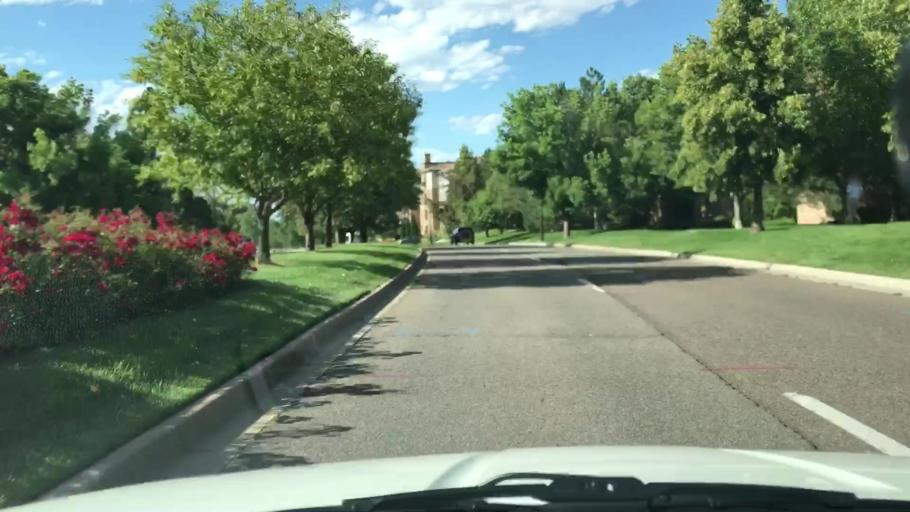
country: US
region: Colorado
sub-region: Arapahoe County
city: Greenwood Village
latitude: 39.6326
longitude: -104.9108
